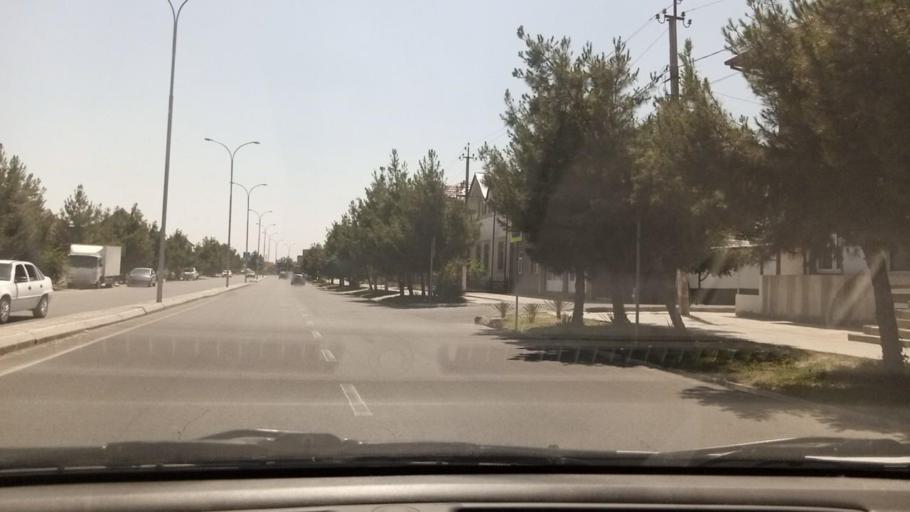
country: UZ
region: Toshkent Shahri
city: Tashkent
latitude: 41.2308
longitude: 69.1844
